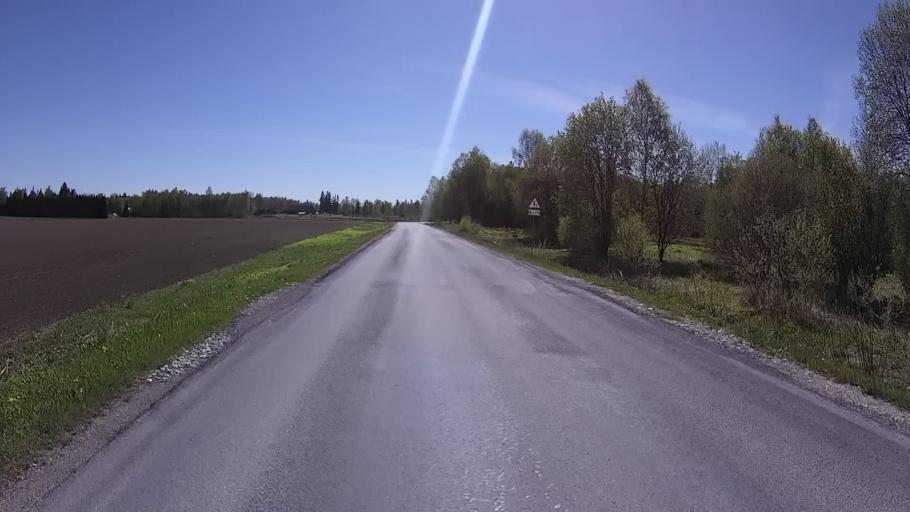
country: EE
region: Harju
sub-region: Raasiku vald
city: Raasiku
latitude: 59.0882
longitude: 25.1764
